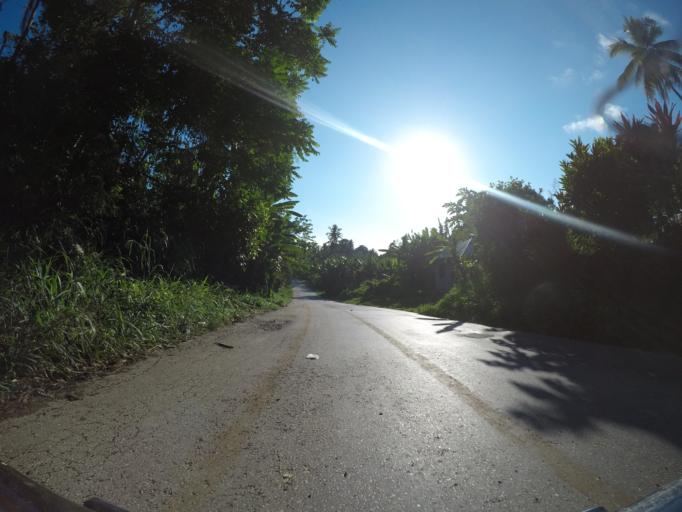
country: TZ
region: Pemba South
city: Mtambile
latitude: -5.3714
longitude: 39.7069
